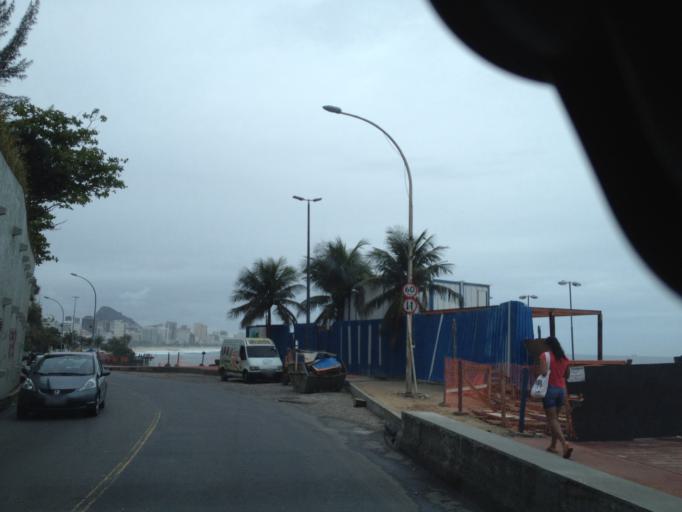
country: BR
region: Rio de Janeiro
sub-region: Rio De Janeiro
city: Rio de Janeiro
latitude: -22.9908
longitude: -43.2295
